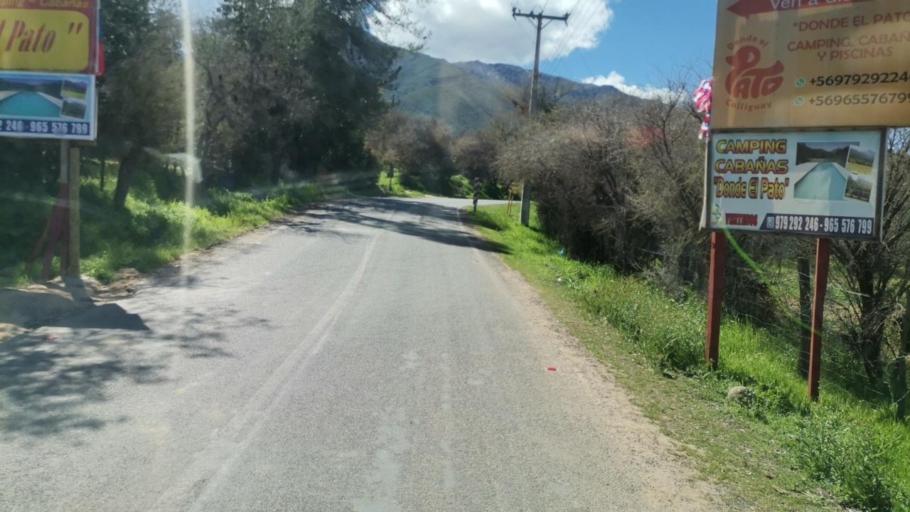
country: CL
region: Valparaiso
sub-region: Provincia de Marga Marga
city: Limache
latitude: -33.1720
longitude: -71.1645
